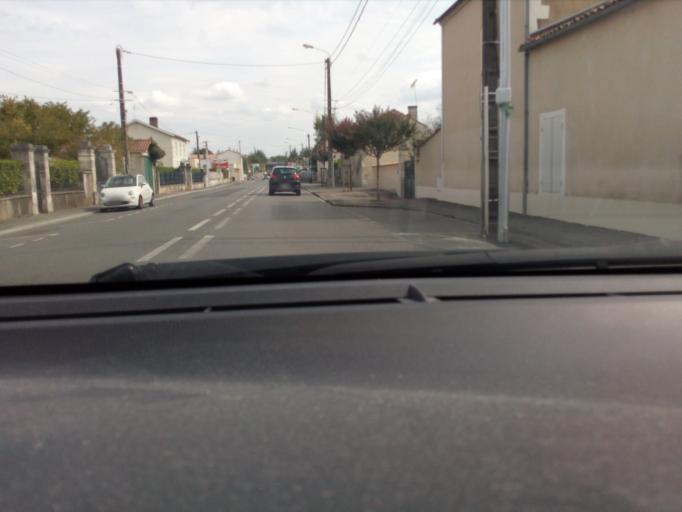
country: FR
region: Poitou-Charentes
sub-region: Departement de la Charente
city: Saint-Yrieix-sur-Charente
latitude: 45.6657
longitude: 0.1246
